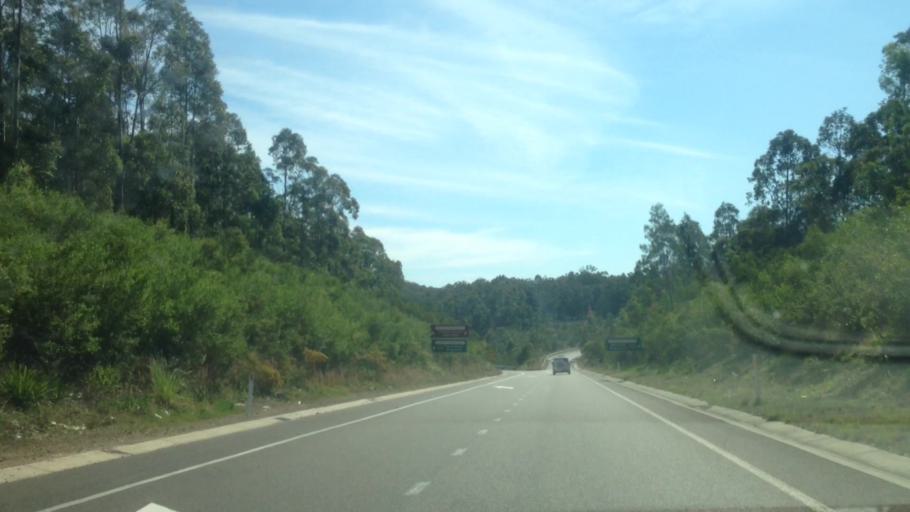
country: AU
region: New South Wales
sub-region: Lake Macquarie Shire
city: Holmesville
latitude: -32.8912
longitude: 151.5964
